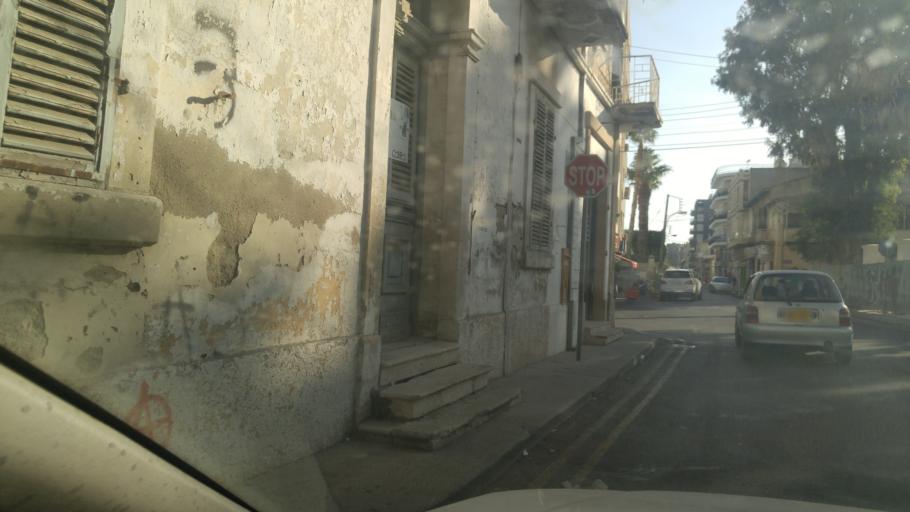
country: CY
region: Limassol
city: Limassol
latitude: 34.6803
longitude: 33.0499
